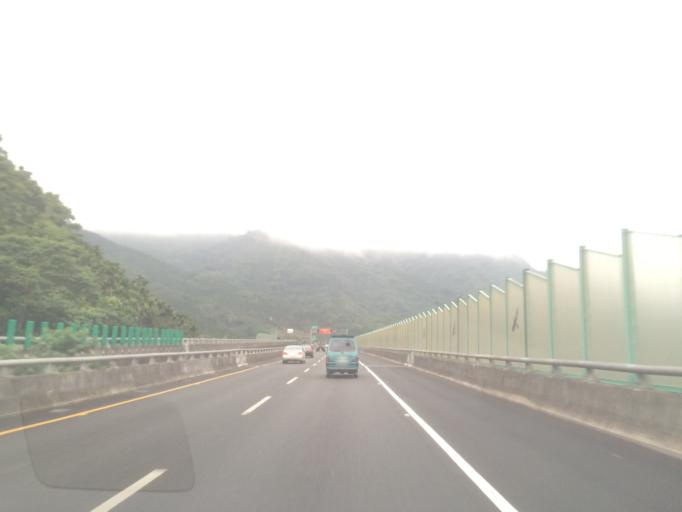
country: TW
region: Taiwan
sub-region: Nantou
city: Puli
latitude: 23.9969
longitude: 120.8493
